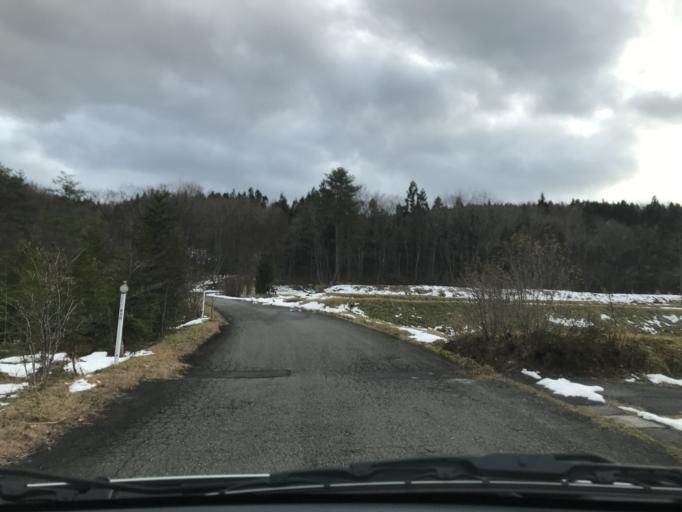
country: JP
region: Iwate
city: Ichinoseki
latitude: 38.9962
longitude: 140.9982
